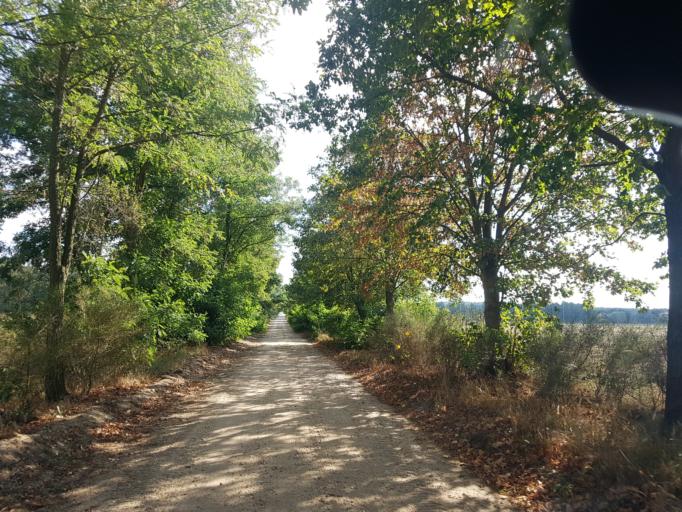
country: DE
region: Brandenburg
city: Gorzke
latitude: 52.0413
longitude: 12.2941
